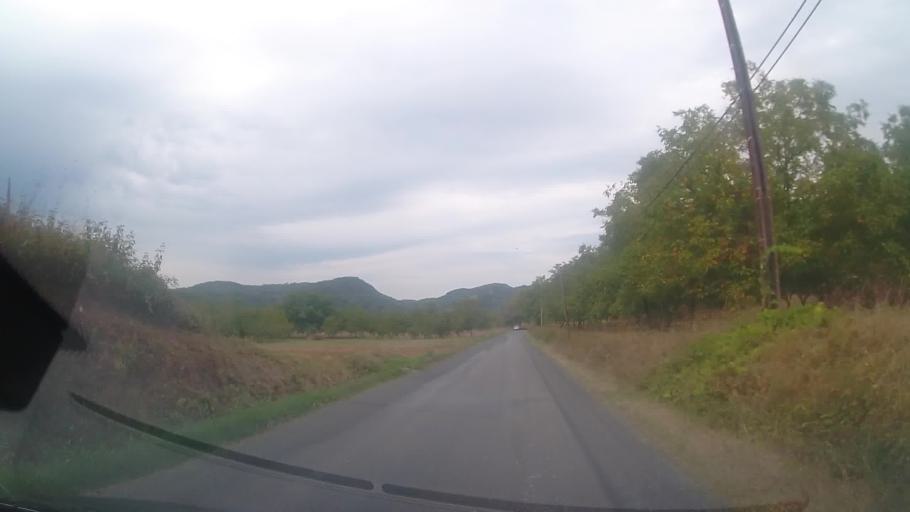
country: FR
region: Aquitaine
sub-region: Departement de la Dordogne
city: Eyvigues-et-Eybenes
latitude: 44.8504
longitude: 1.3648
